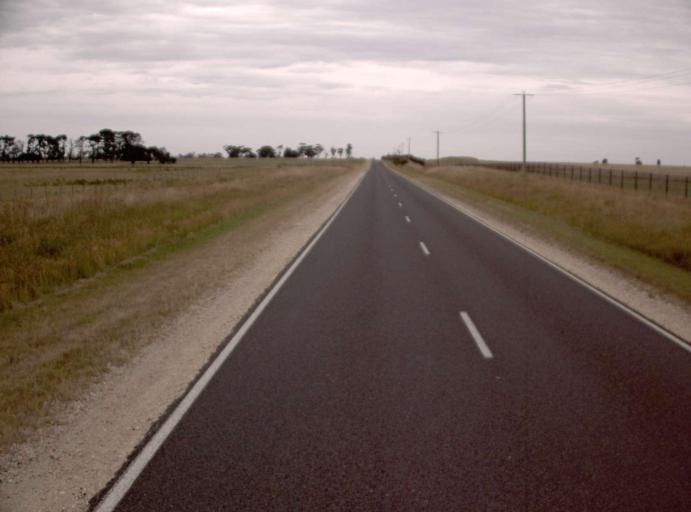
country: AU
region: Victoria
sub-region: Wellington
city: Sale
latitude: -38.1776
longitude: 147.2164
